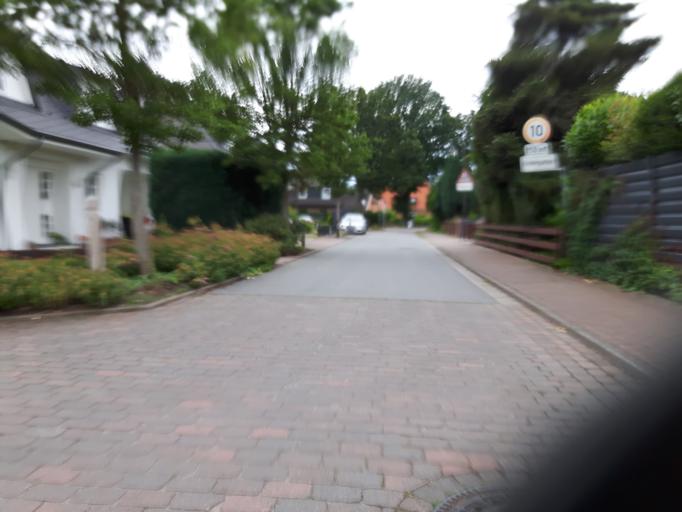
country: DE
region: Lower Saxony
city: Stuhr
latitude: 53.0322
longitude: 8.6953
